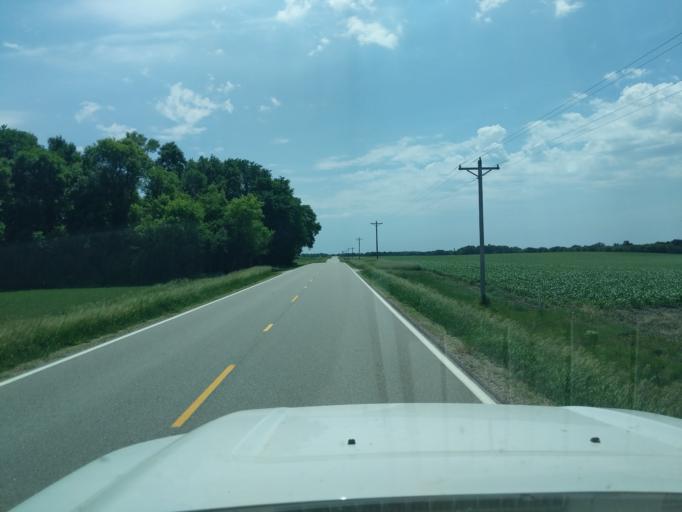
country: US
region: Minnesota
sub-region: Yellow Medicine County
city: Granite Falls
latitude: 44.7655
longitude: -95.4023
